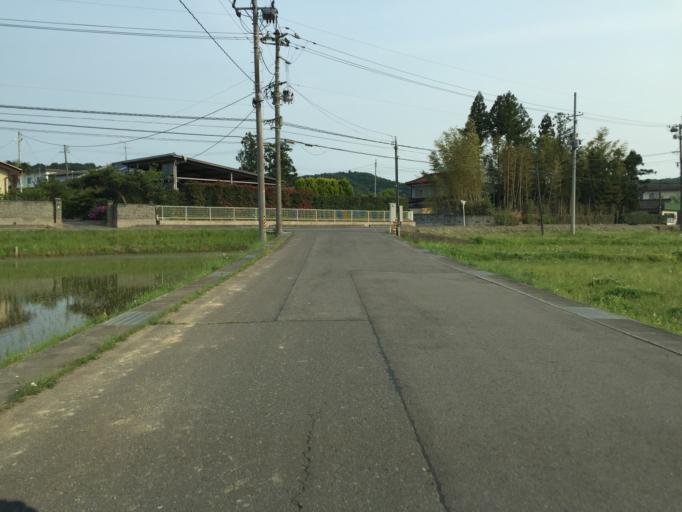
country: JP
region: Fukushima
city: Fukushima-shi
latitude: 37.7134
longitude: 140.4357
